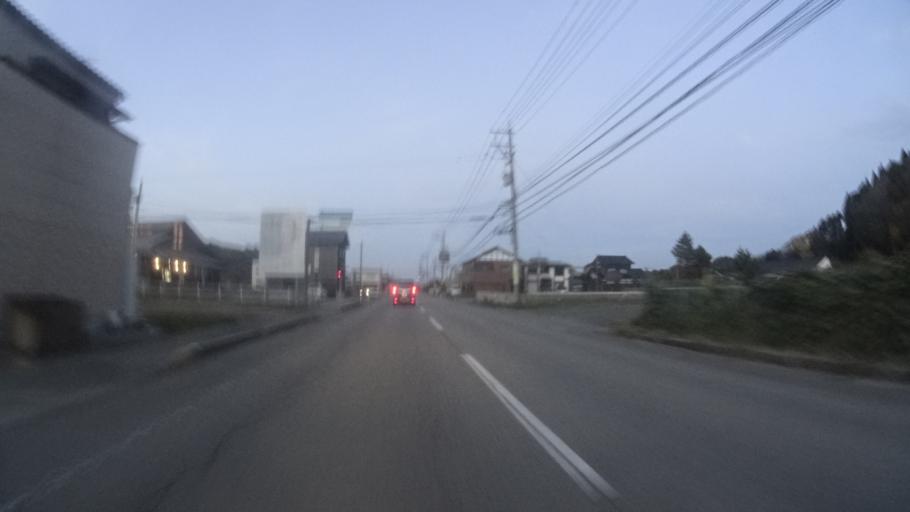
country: JP
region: Ishikawa
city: Nanao
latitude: 37.3805
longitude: 136.8860
